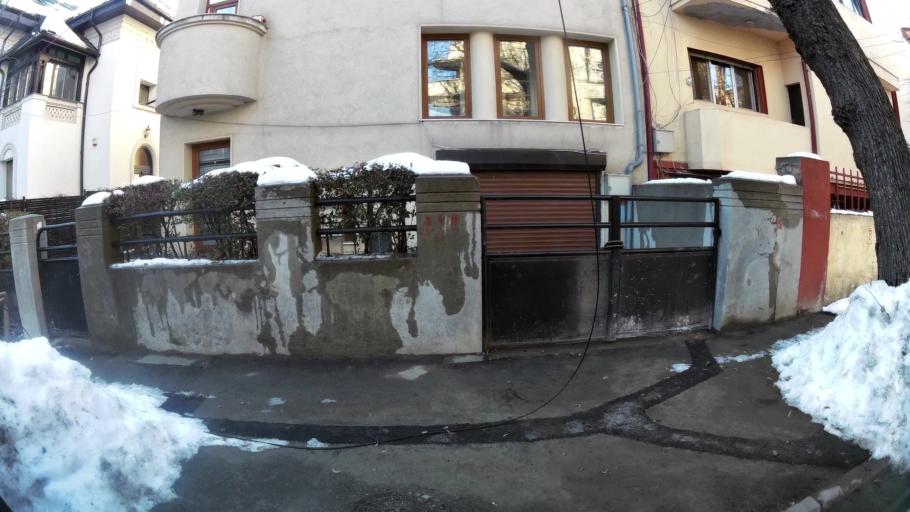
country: RO
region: Bucuresti
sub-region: Municipiul Bucuresti
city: Bucuresti
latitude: 44.4301
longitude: 26.0714
